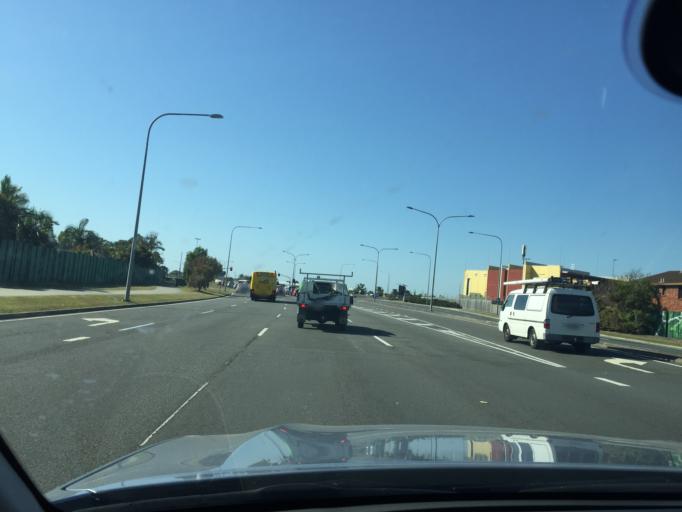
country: AU
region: Queensland
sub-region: Gold Coast
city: Clear Island Waters
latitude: -28.0340
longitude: 153.4067
